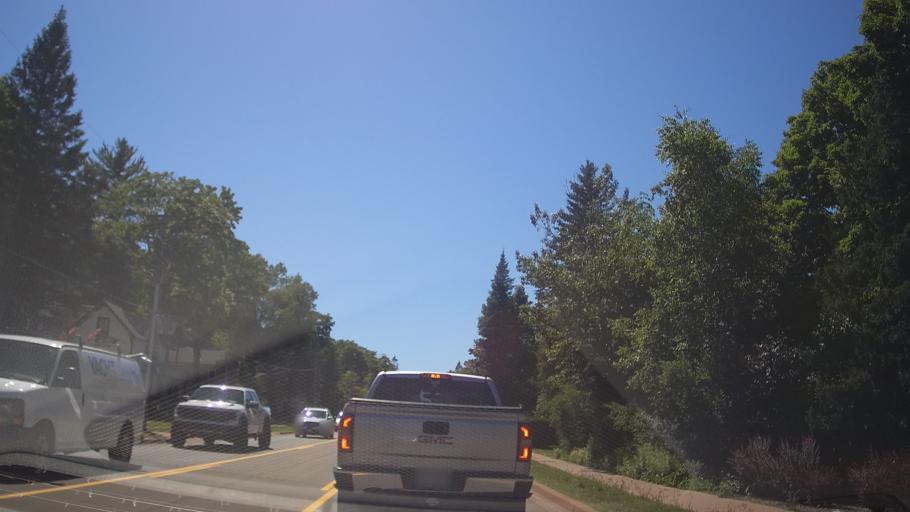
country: US
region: Michigan
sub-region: Emmet County
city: Petoskey
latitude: 45.3860
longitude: -84.9294
